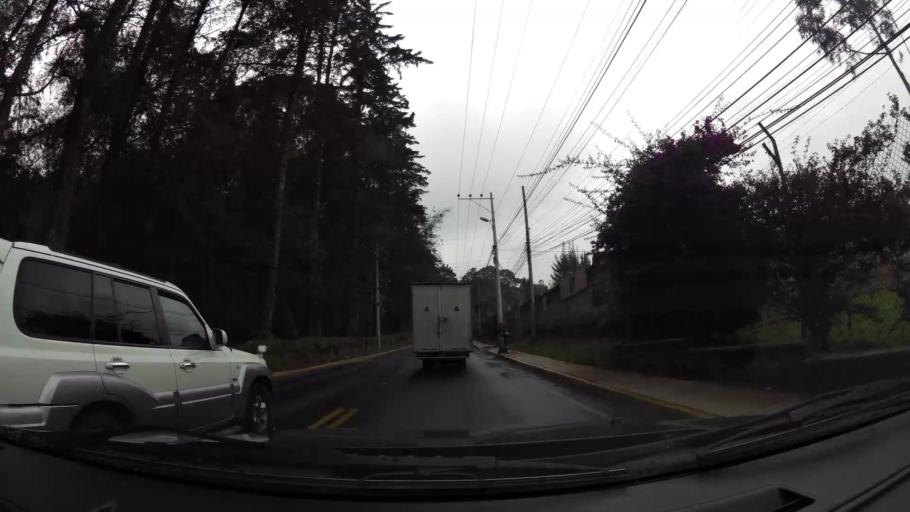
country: EC
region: Pichincha
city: Quito
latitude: -0.2676
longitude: -78.4688
